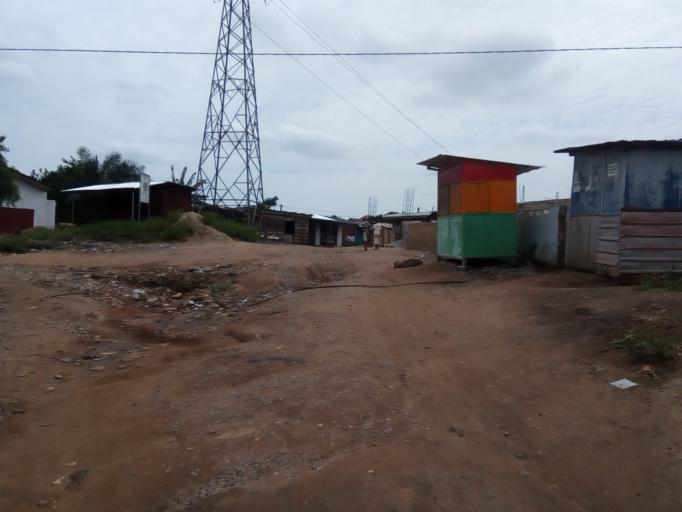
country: GH
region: Eastern
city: Nsawam
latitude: 5.7801
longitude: -0.3366
